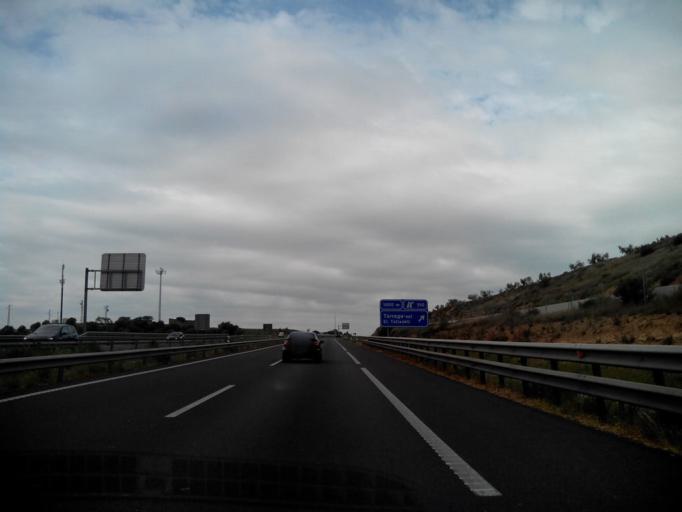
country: ES
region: Catalonia
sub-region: Provincia de Lleida
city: Tarrega
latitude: 41.6603
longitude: 1.1860
